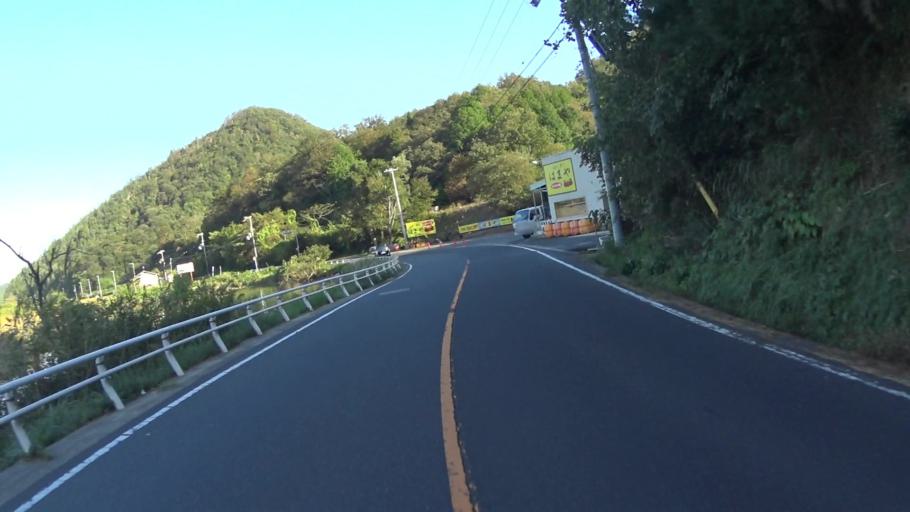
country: JP
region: Hyogo
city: Toyooka
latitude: 35.6053
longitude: 134.9091
